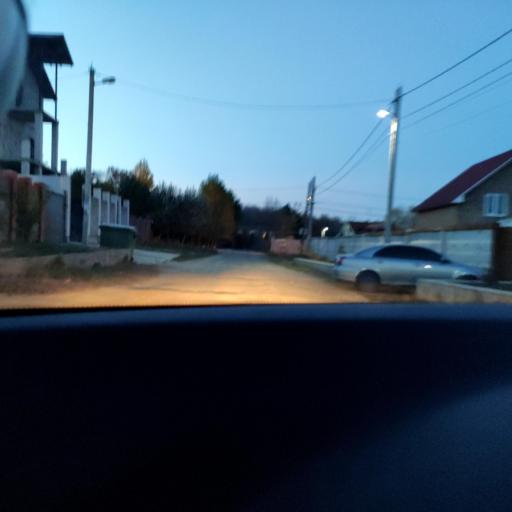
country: RU
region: Samara
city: Petra-Dubrava
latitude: 53.3142
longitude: 50.2748
